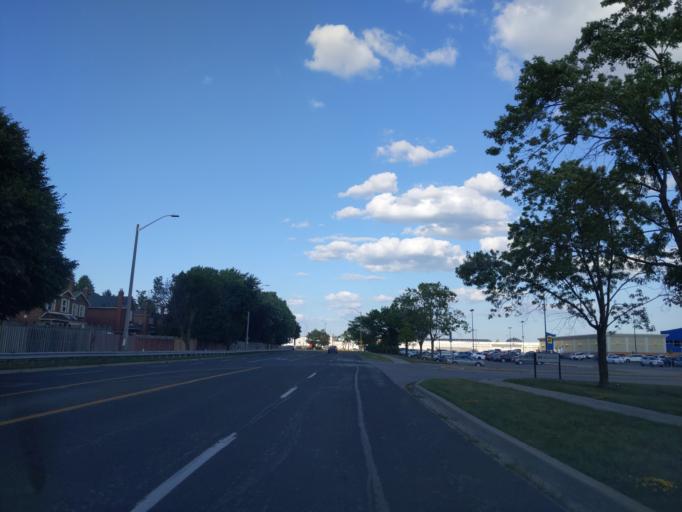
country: CA
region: Ontario
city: Markham
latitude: 43.8694
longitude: -79.2918
